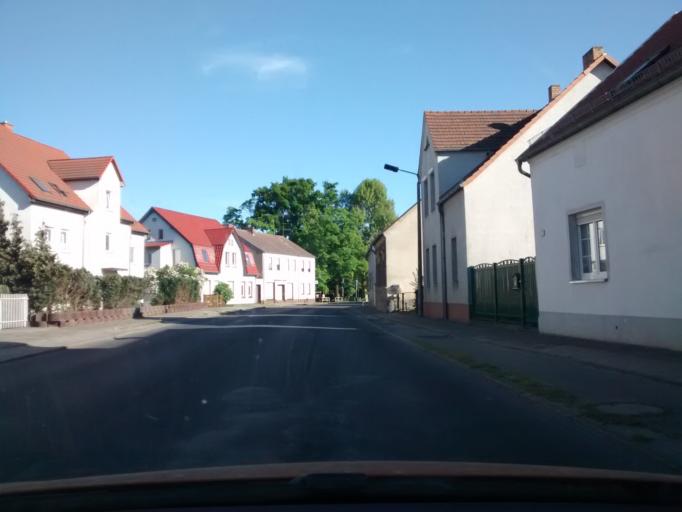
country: DE
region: Brandenburg
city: Furstenwalde
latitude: 52.3427
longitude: 14.0737
